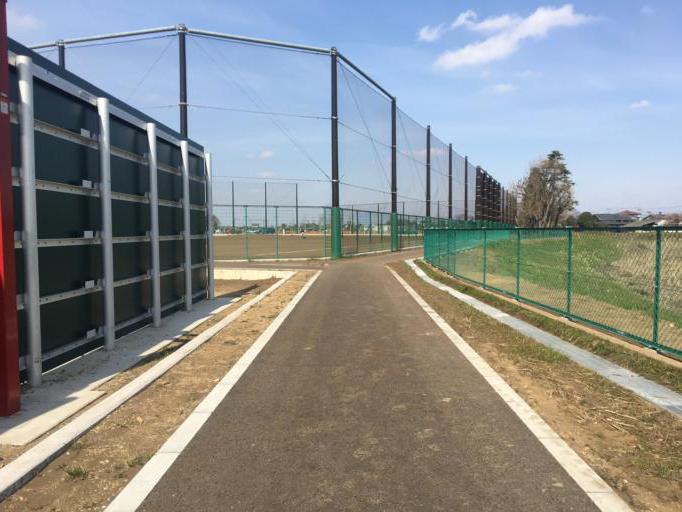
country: JP
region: Saitama
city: Oi
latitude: 35.8709
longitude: 139.5505
